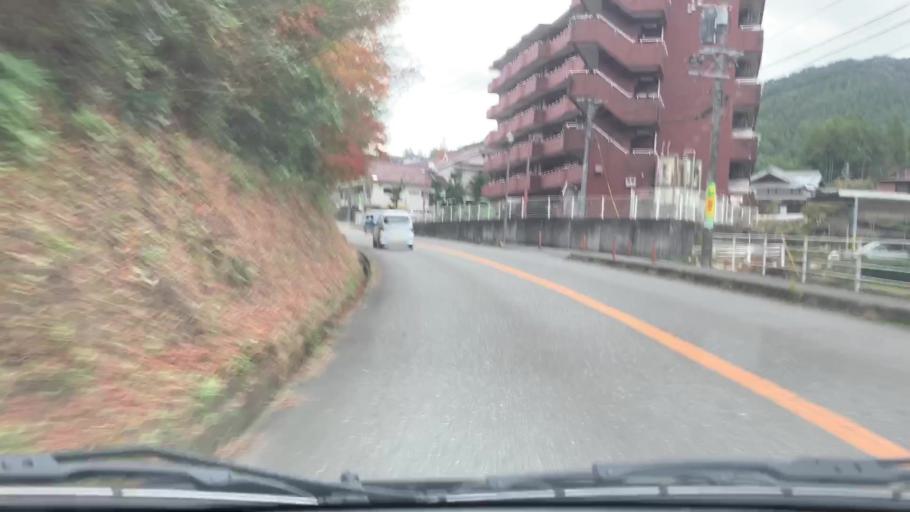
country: JP
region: Saga Prefecture
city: Ureshinomachi-shimojuku
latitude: 33.1037
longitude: 129.9782
